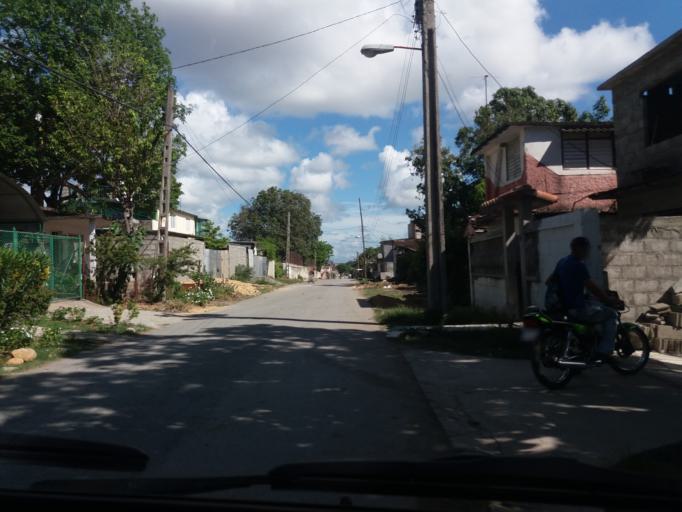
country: CU
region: Cienfuegos
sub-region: Municipio de Cienfuegos
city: Cienfuegos
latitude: 22.1482
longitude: -80.4240
